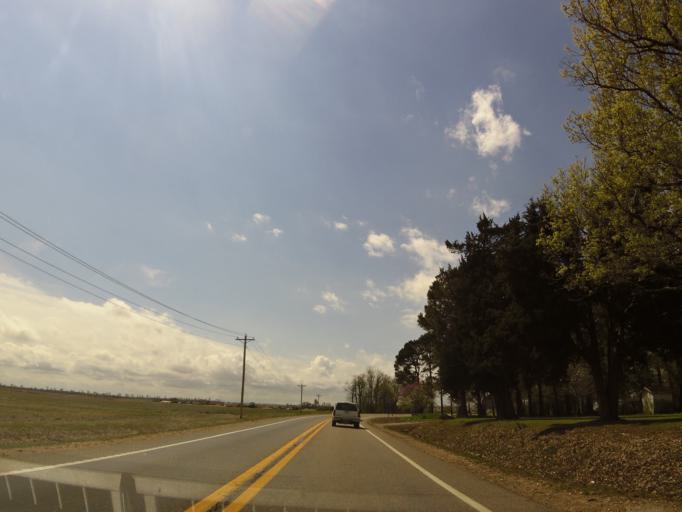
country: US
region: Arkansas
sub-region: Clay County
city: Corning
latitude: 36.3811
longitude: -90.5200
